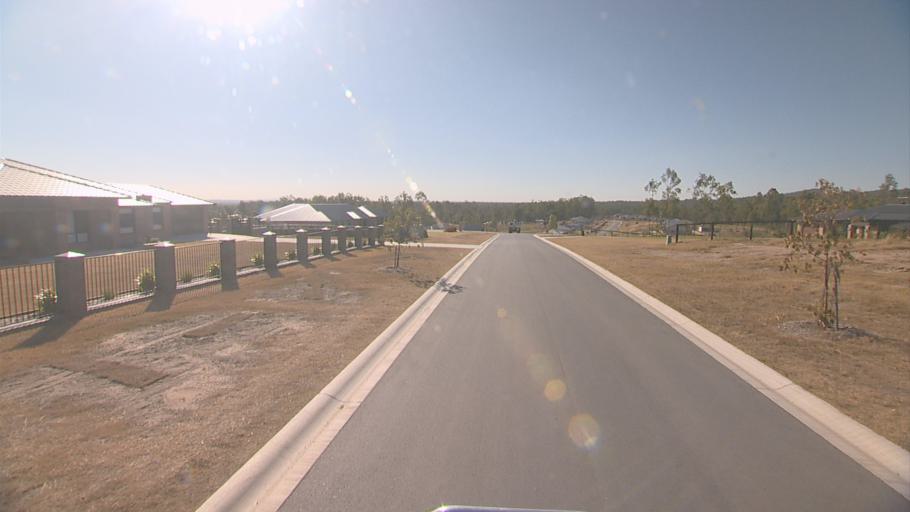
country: AU
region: Queensland
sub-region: Logan
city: Cedar Vale
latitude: -27.8721
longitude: 153.0520
